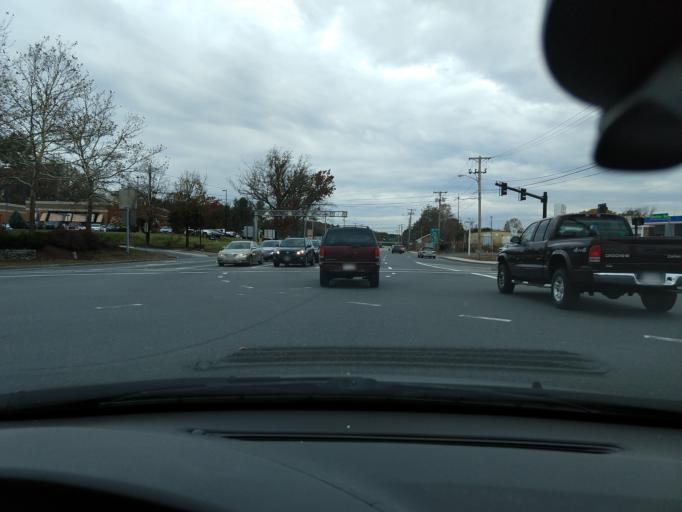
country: US
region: Massachusetts
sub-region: Middlesex County
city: Westford
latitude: 42.5663
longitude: -71.4239
